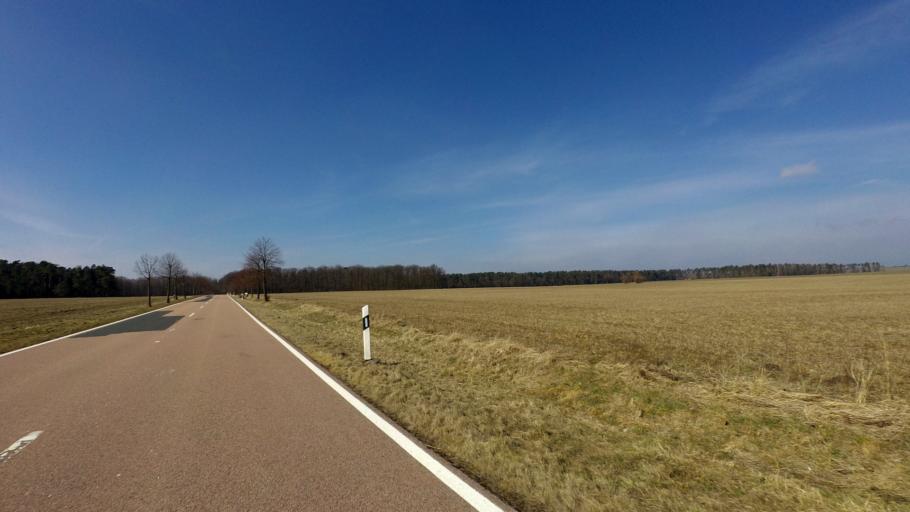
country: DE
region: Saxony-Anhalt
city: Nudersdorf
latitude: 51.9489
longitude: 12.5834
